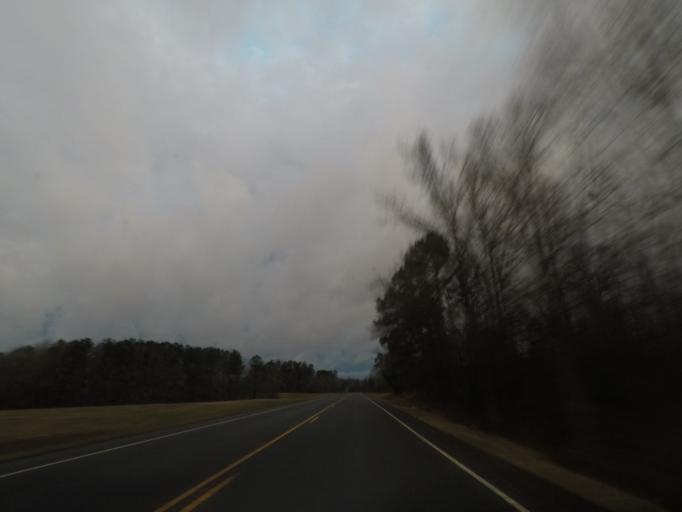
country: US
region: North Carolina
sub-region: Alamance County
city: Mebane
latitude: 36.2228
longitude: -79.1840
